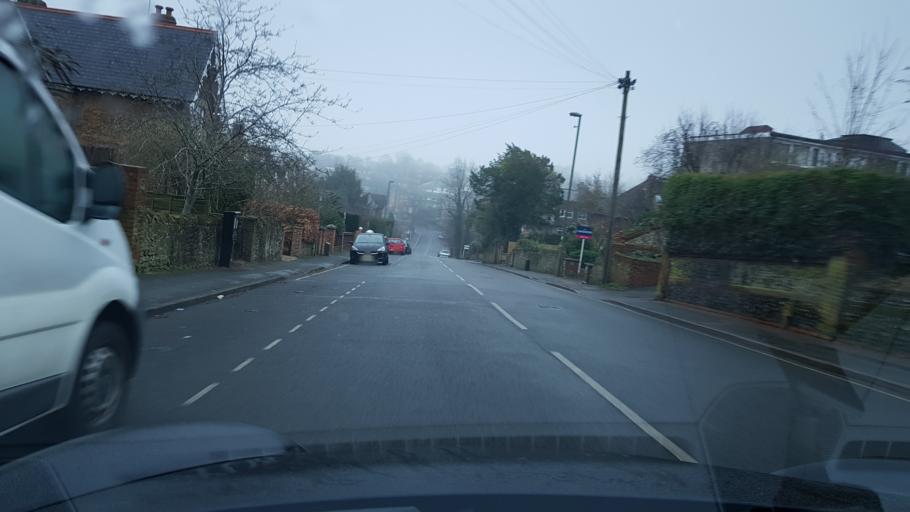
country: GB
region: England
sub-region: Surrey
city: Guildford
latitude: 51.2362
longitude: -0.5647
